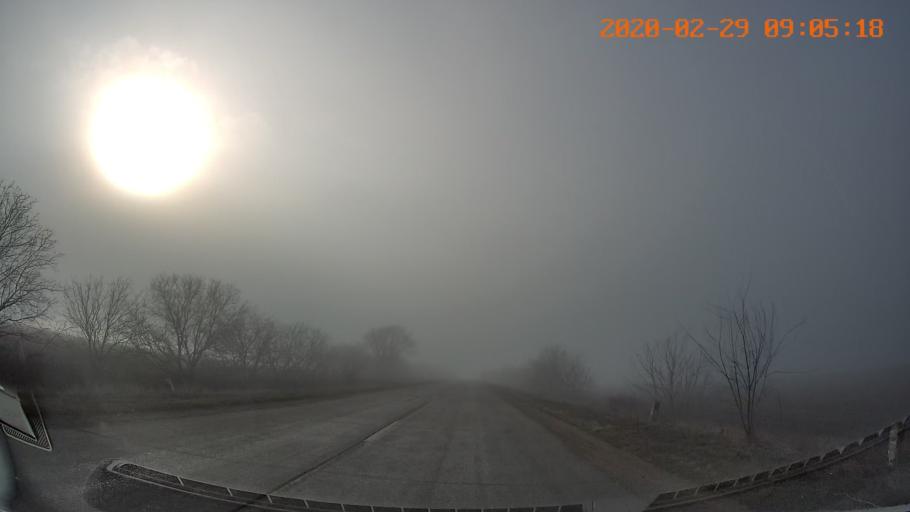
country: MD
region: Telenesti
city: Tiraspolul Nou
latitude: 46.8911
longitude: 29.7396
